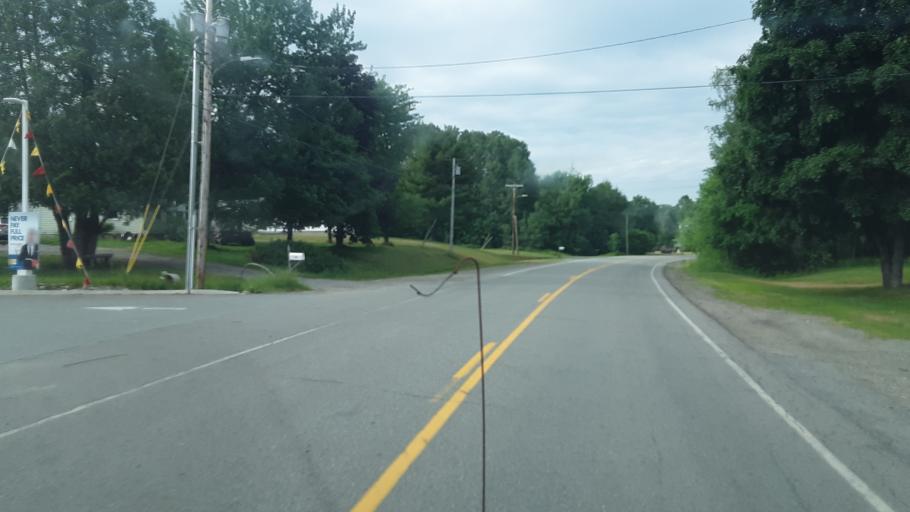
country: US
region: Maine
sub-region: Penobscot County
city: Lincoln
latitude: 45.5024
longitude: -68.3563
